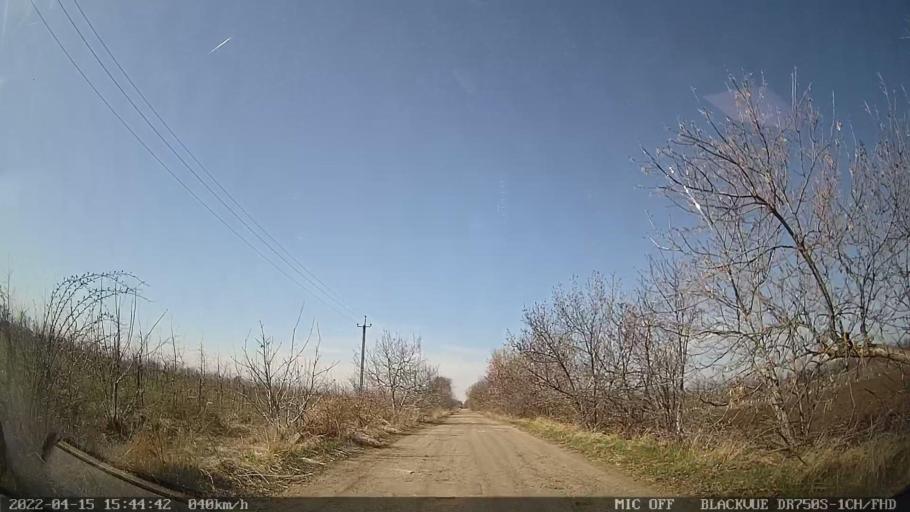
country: MD
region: Raionul Ocnita
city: Otaci
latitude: 48.3718
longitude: 27.9214
